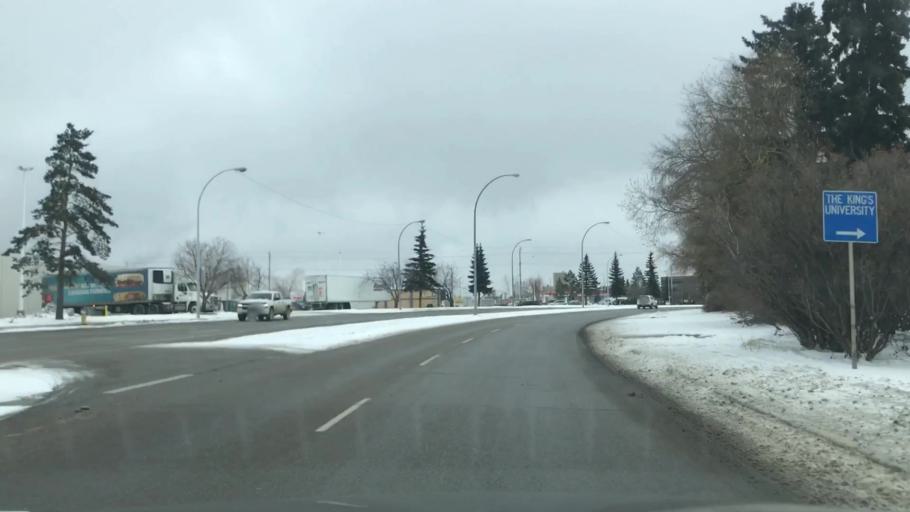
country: CA
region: Alberta
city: Edmonton
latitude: 53.5383
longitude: -113.4225
